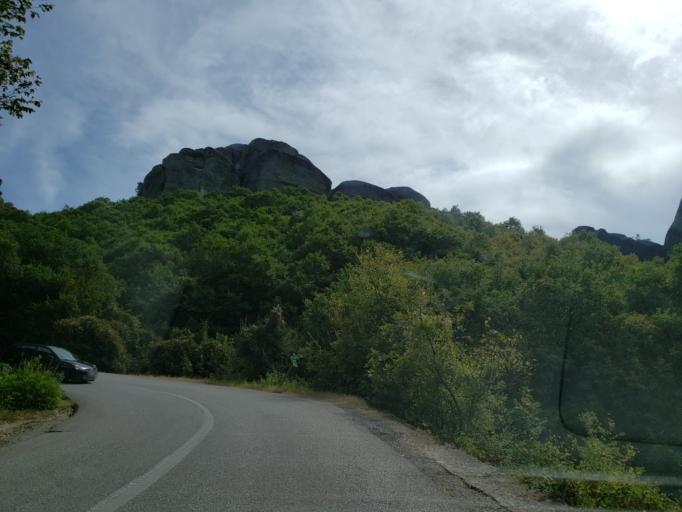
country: GR
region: Thessaly
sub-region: Trikala
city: Kastraki
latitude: 39.7188
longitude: 21.6333
